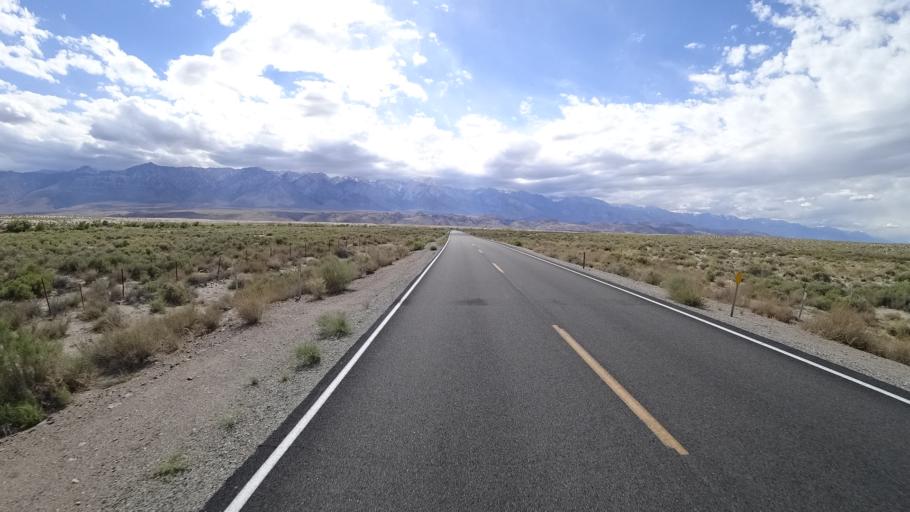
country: US
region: California
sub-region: Inyo County
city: Lone Pine
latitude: 36.5742
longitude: -117.9999
